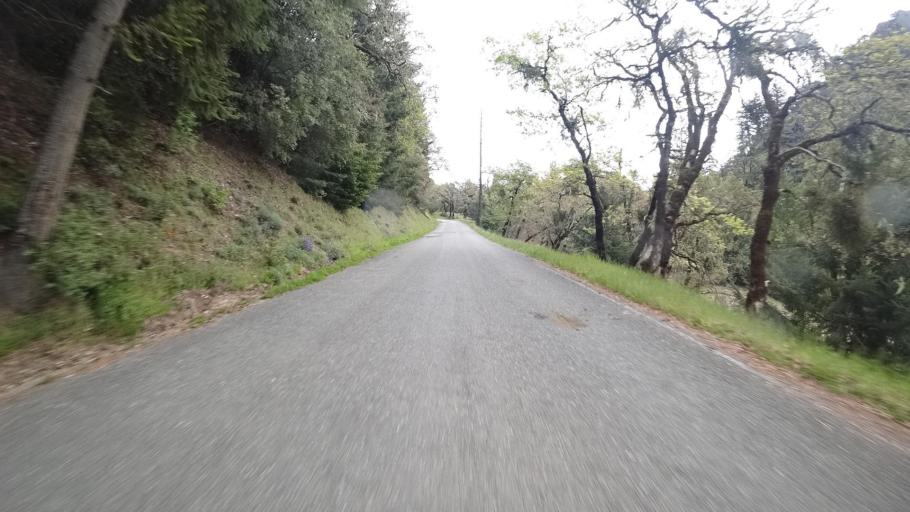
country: US
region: California
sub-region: Humboldt County
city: Redway
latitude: 40.1552
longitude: -123.5540
